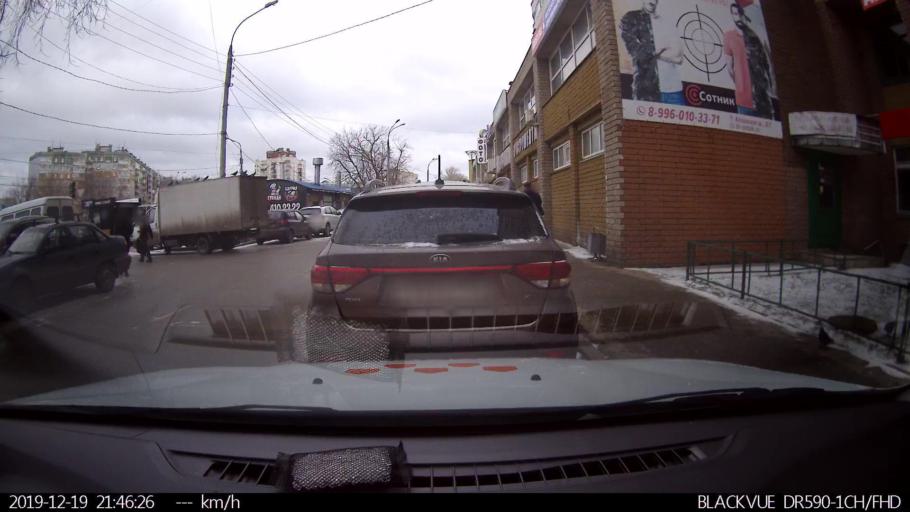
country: RU
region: Nizjnij Novgorod
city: Afonino
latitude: 56.2671
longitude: 44.0595
